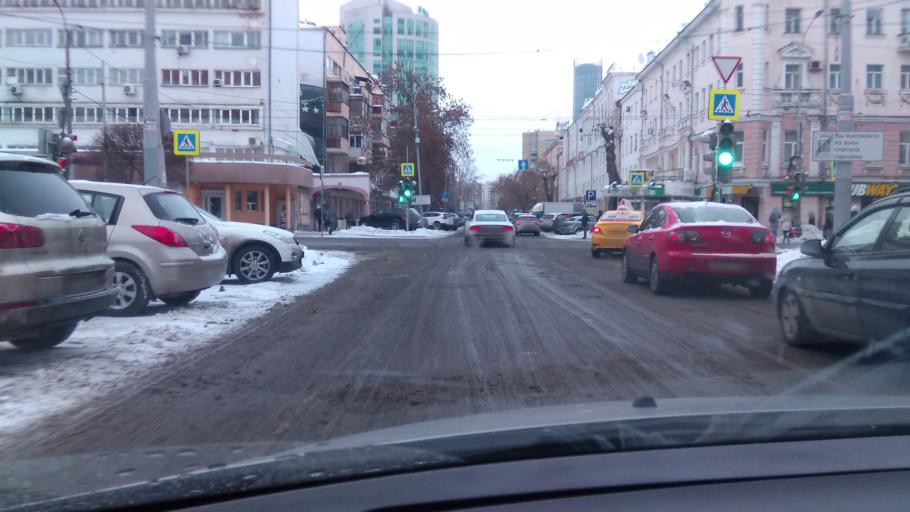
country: RU
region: Sverdlovsk
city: Yekaterinburg
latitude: 56.8329
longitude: 60.5925
